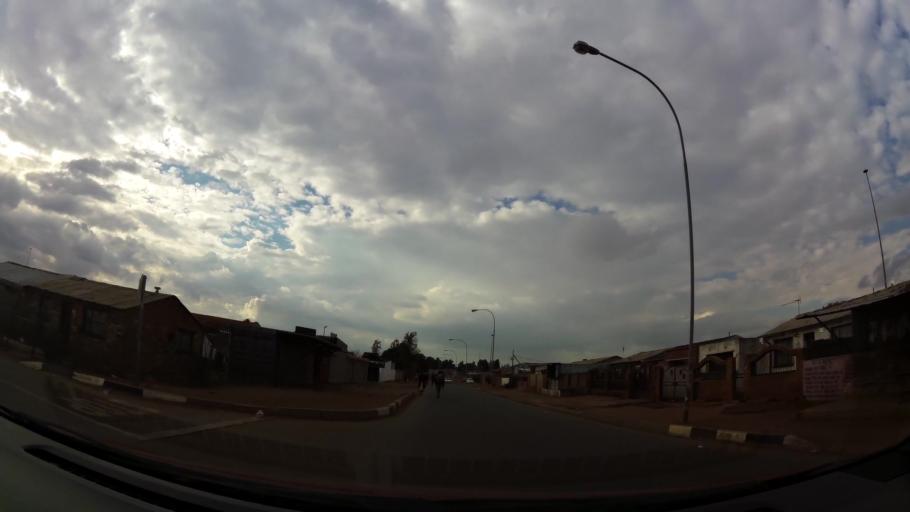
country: ZA
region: Gauteng
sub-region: City of Johannesburg Metropolitan Municipality
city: Soweto
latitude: -26.2521
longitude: 27.8231
